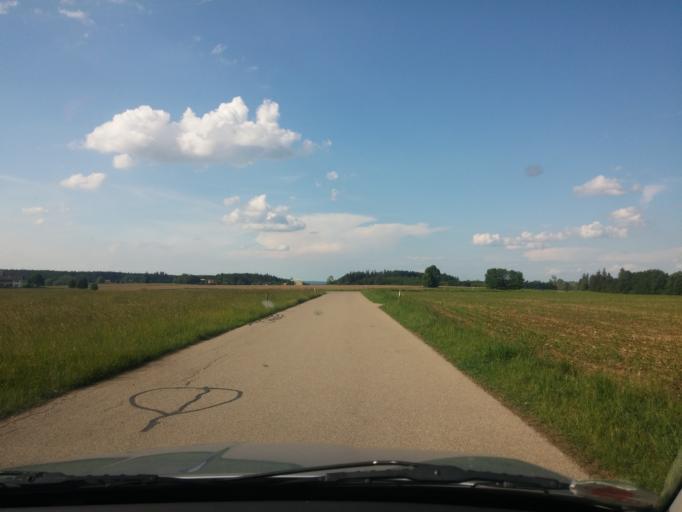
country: DE
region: Bavaria
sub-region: Swabia
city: Woringen
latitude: 47.8860
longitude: 10.1970
